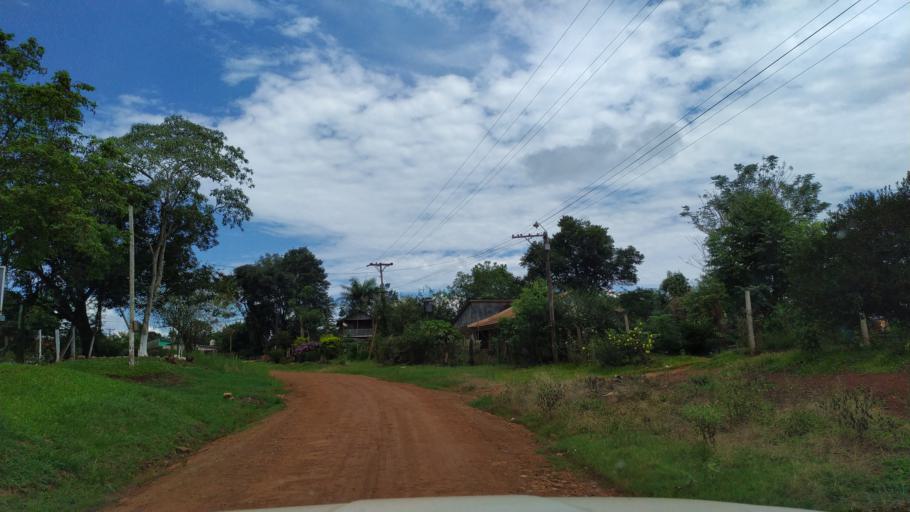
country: AR
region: Misiones
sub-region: Departamento de Eldorado
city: Eldorado
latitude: -26.5212
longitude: -54.5966
